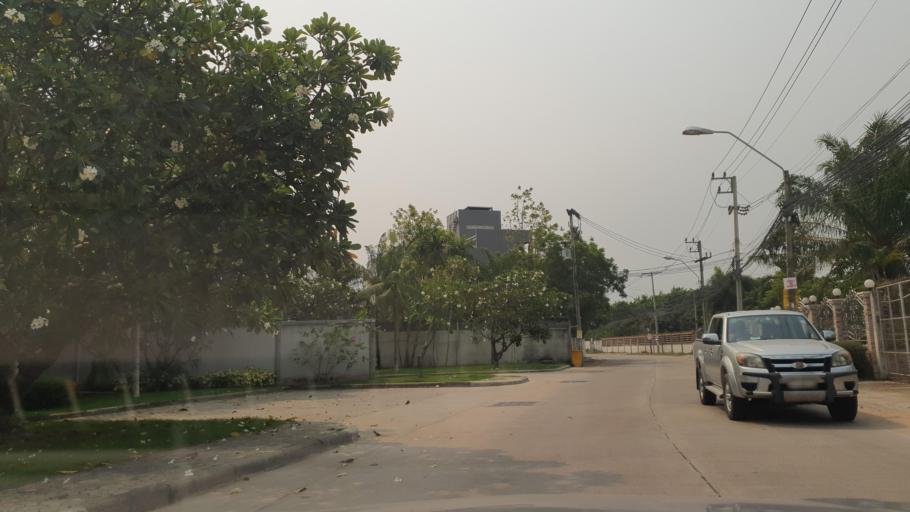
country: TH
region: Chon Buri
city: Phatthaya
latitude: 12.8927
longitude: 100.8912
